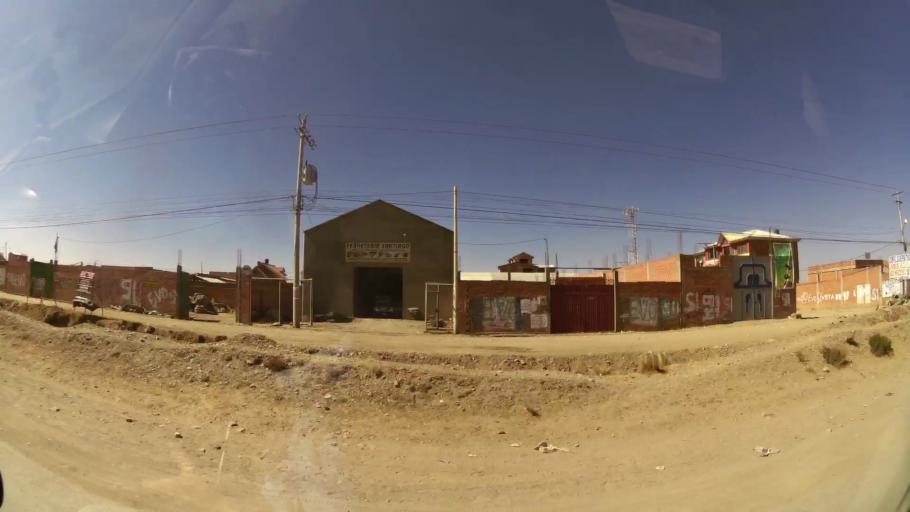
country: BO
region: La Paz
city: La Paz
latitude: -16.5592
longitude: -68.2132
